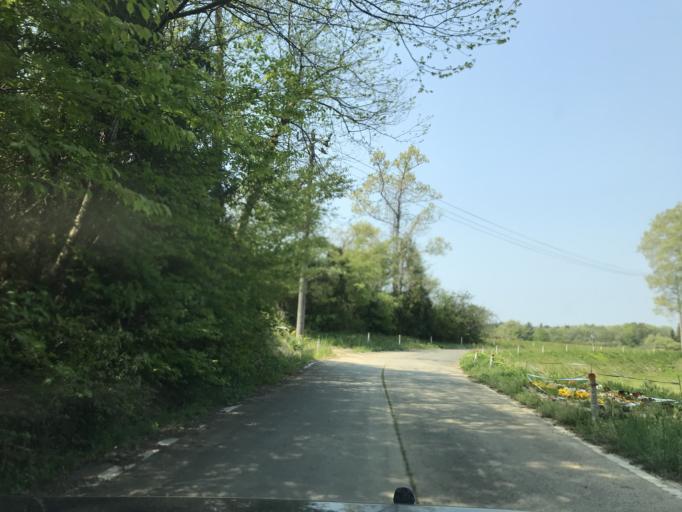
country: JP
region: Iwate
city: Ichinoseki
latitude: 38.8563
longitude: 141.0693
